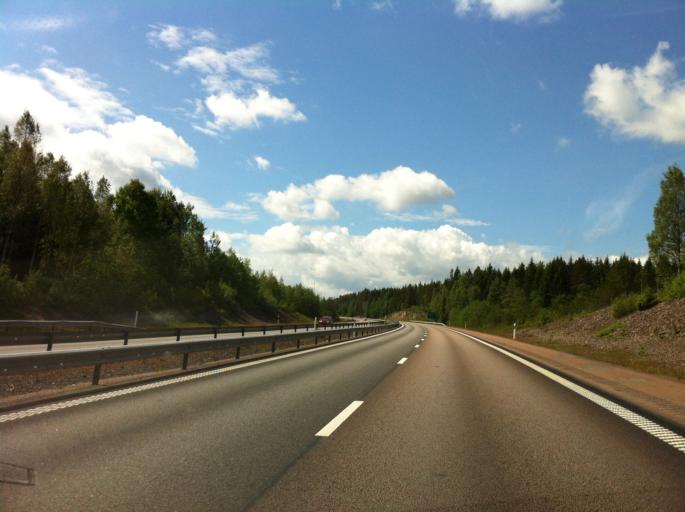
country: SE
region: Vaermland
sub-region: Grums Kommun
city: Slottsbron
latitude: 59.2774
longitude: 13.0184
